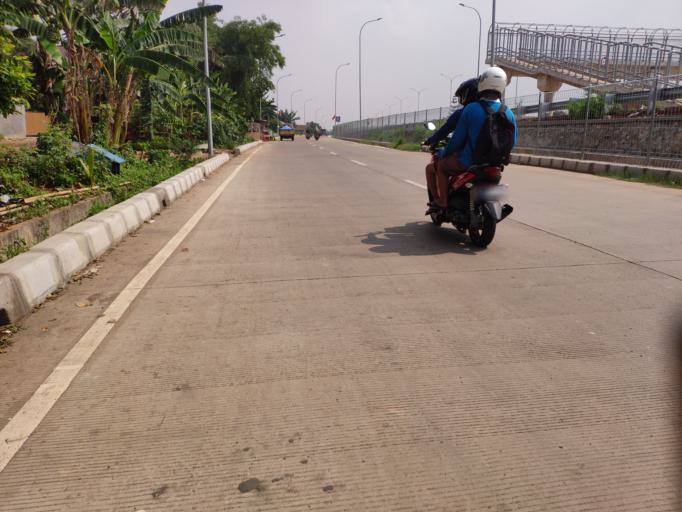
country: ID
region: West Java
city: Pamulang
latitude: -6.3281
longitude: 106.8005
